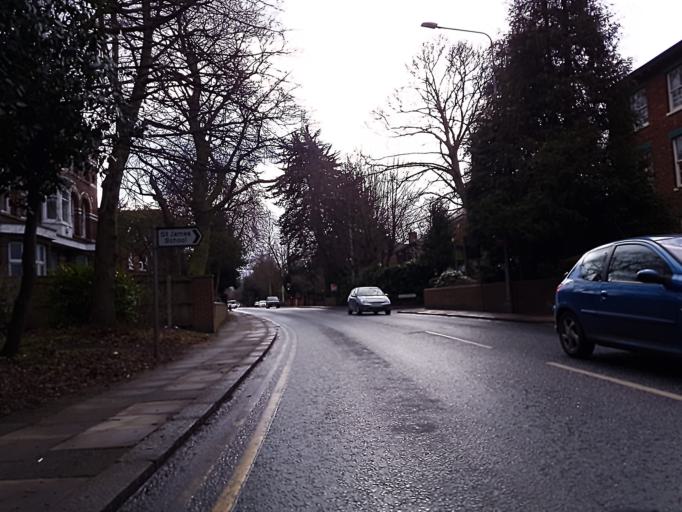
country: GB
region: England
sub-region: North East Lincolnshire
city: Grimbsy
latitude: 53.5608
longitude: -0.0922
